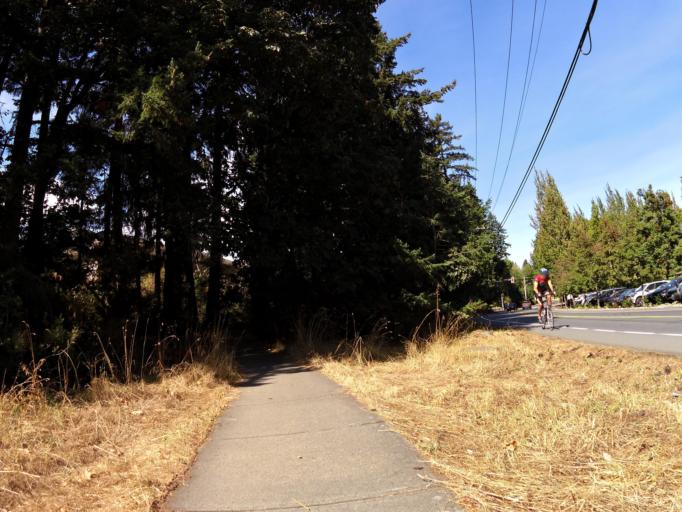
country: CA
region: British Columbia
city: Victoria
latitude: 48.5290
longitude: -123.3733
